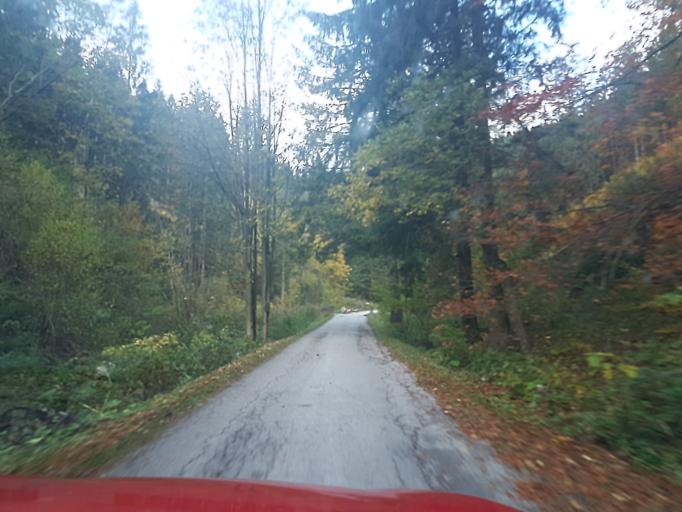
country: SK
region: Zilinsky
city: Ruzomberok
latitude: 48.9956
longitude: 19.2629
